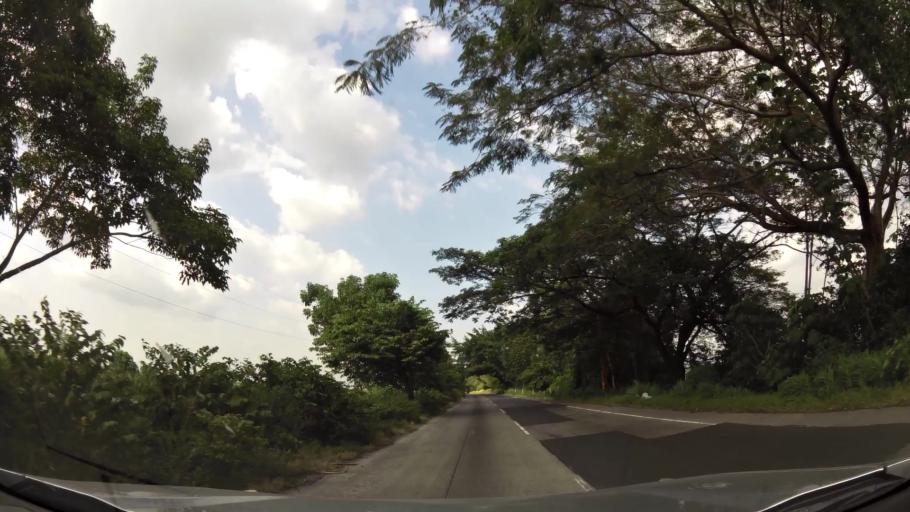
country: GT
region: Escuintla
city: Puerto San Jose
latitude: 14.0526
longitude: -90.7763
